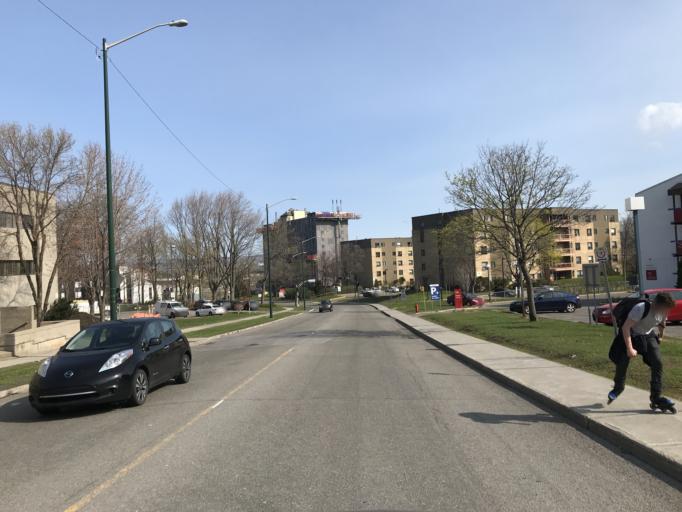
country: CA
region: Quebec
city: L'Ancienne-Lorette
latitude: 46.7882
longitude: -71.2817
